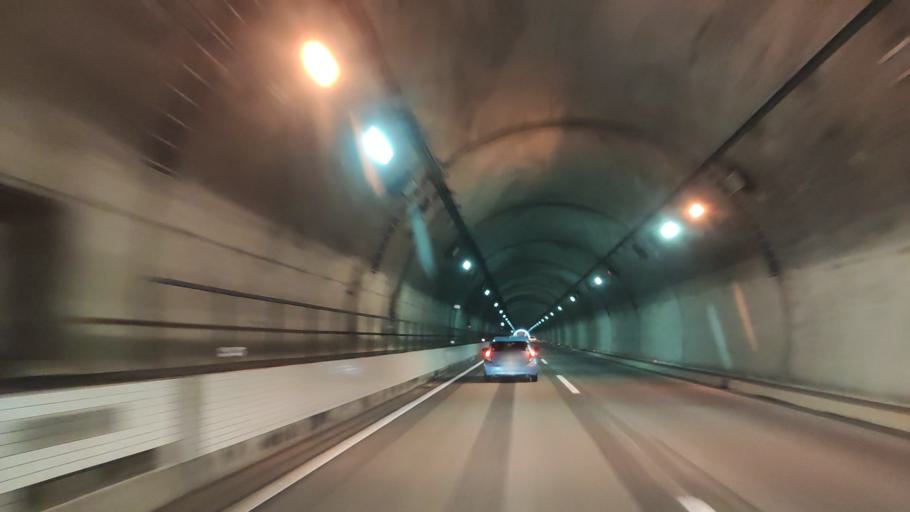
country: JP
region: Ehime
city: Saijo
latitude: 33.8749
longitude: 133.0767
